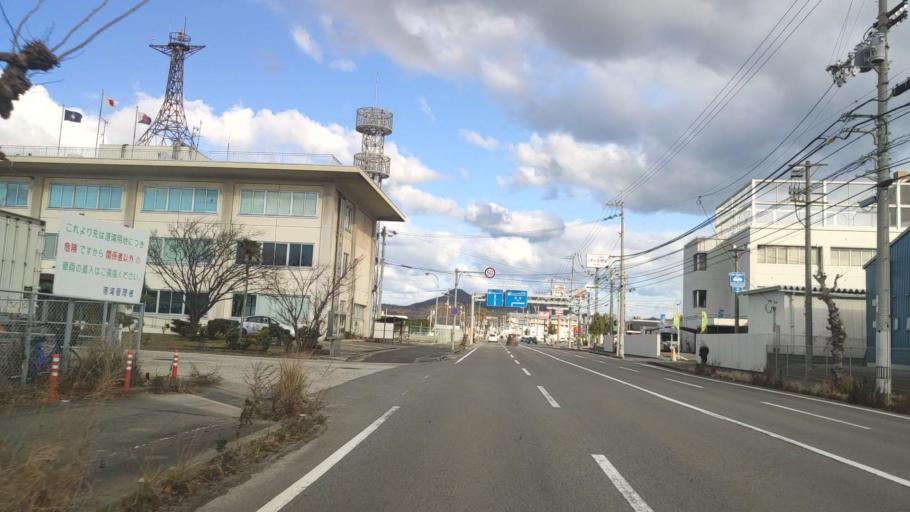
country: JP
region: Ehime
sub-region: Shikoku-chuo Shi
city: Matsuyama
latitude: 33.8557
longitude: 132.7128
